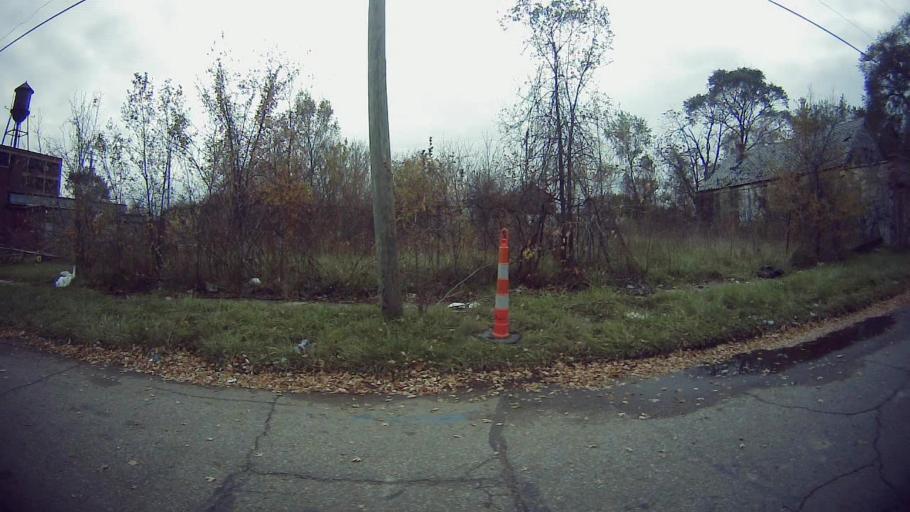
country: US
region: Michigan
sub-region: Wayne County
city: Hamtramck
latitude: 42.3903
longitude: -83.0363
